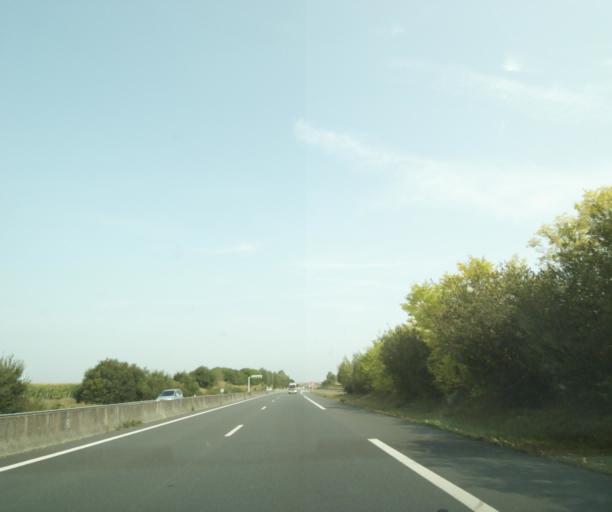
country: FR
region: Pays de la Loire
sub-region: Departement de la Sarthe
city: Beaumont-sur-Sarthe
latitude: 48.2447
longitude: 0.1643
